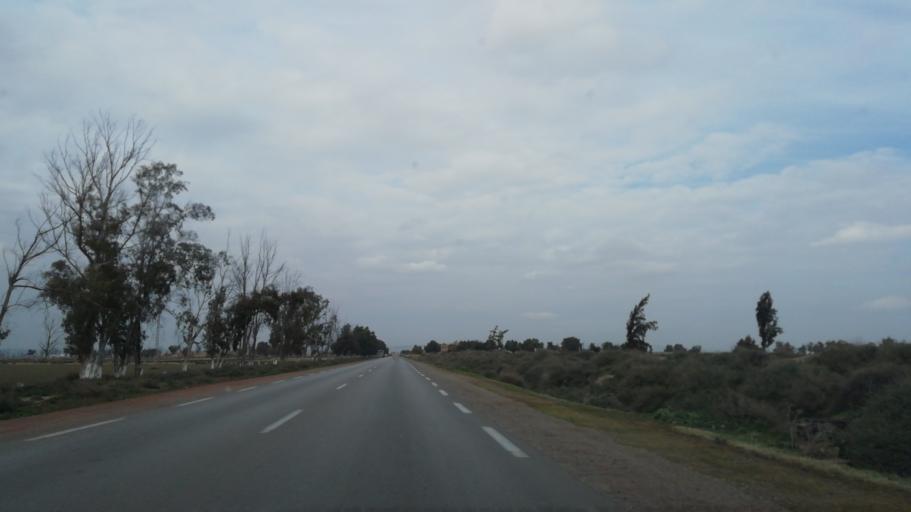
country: DZ
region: Mostaganem
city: Mostaganem
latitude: 35.6791
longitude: 0.0571
